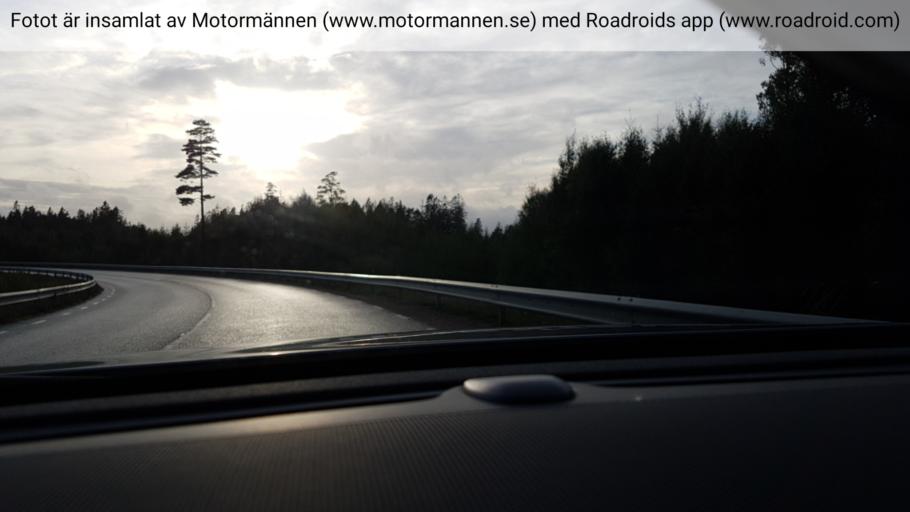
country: SE
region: Vaestra Goetaland
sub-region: Trollhattan
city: Trollhattan
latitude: 58.3392
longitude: 12.2376
